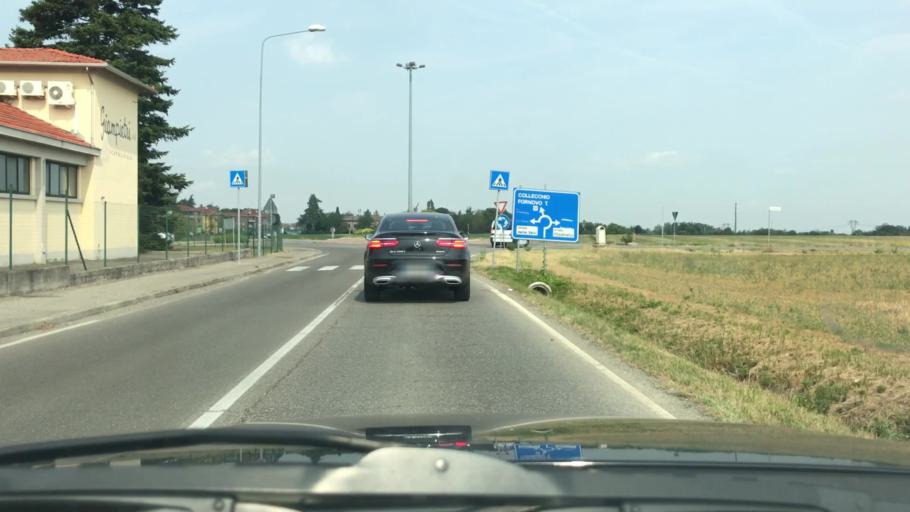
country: IT
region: Emilia-Romagna
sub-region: Provincia di Parma
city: Collecchio
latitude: 44.7436
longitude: 10.2250
